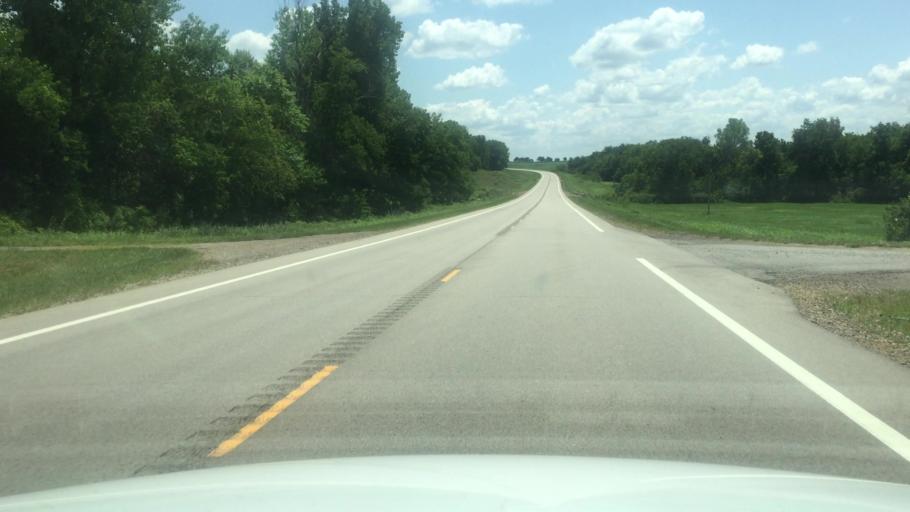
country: US
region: Kansas
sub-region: Brown County
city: Horton
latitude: 39.6239
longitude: -95.3501
